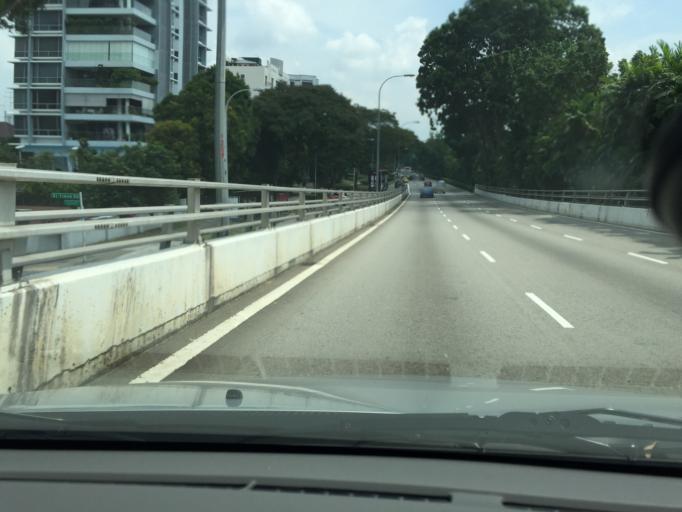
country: SG
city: Singapore
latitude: 1.3210
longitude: 103.8241
